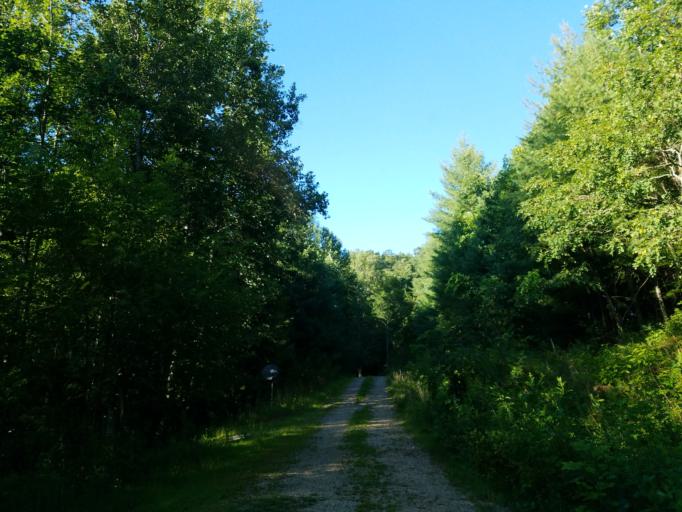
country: US
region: Georgia
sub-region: Union County
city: Blairsville
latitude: 34.7610
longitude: -84.0955
